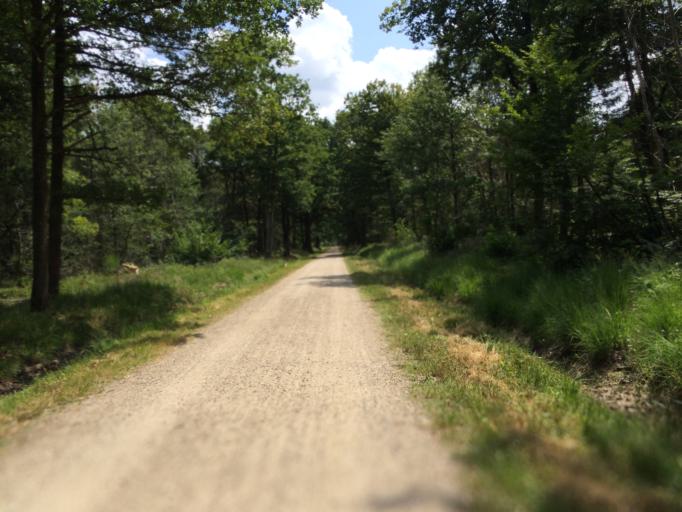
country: FR
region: Ile-de-France
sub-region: Departement de l'Essonne
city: Brunoy
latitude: 48.6719
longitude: 2.4958
